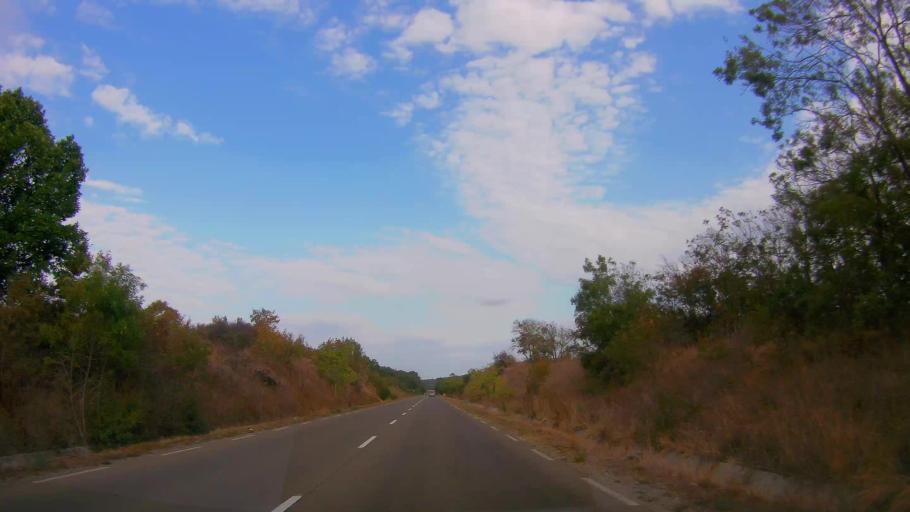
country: BG
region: Burgas
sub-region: Obshtina Sozopol
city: Sozopol
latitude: 42.3492
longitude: 27.7122
